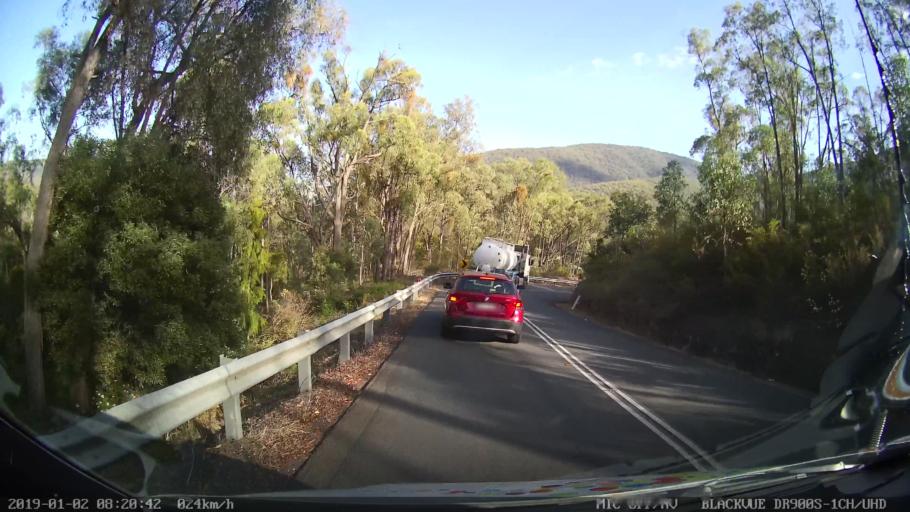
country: AU
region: New South Wales
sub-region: Tumut Shire
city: Tumut
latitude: -35.5715
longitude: 148.3242
